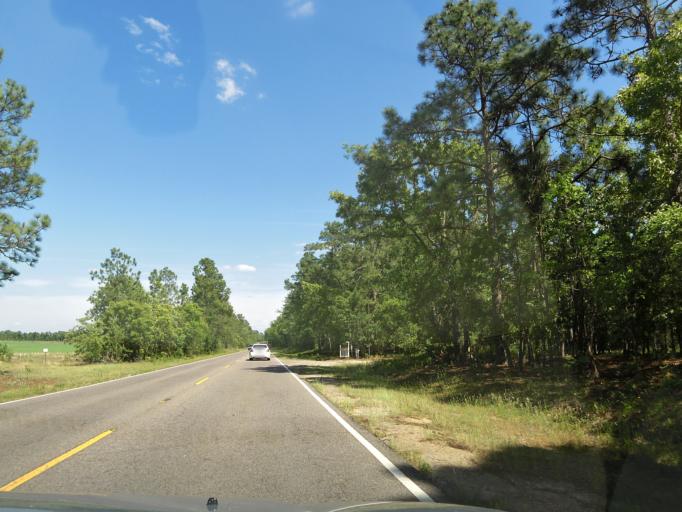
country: US
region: South Carolina
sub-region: Aiken County
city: New Ellenton
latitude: 33.5071
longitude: -81.5494
